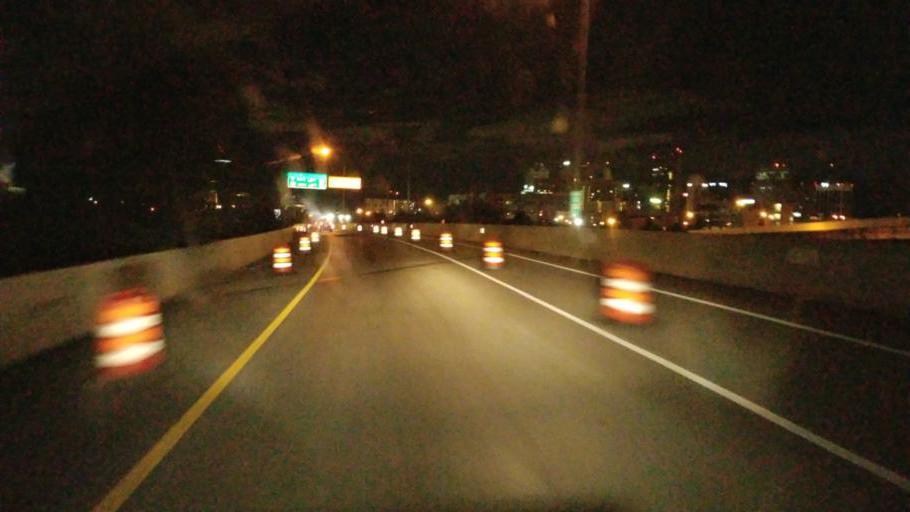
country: US
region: Ohio
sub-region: Franklin County
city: Columbus
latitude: 39.9555
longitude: -82.9815
